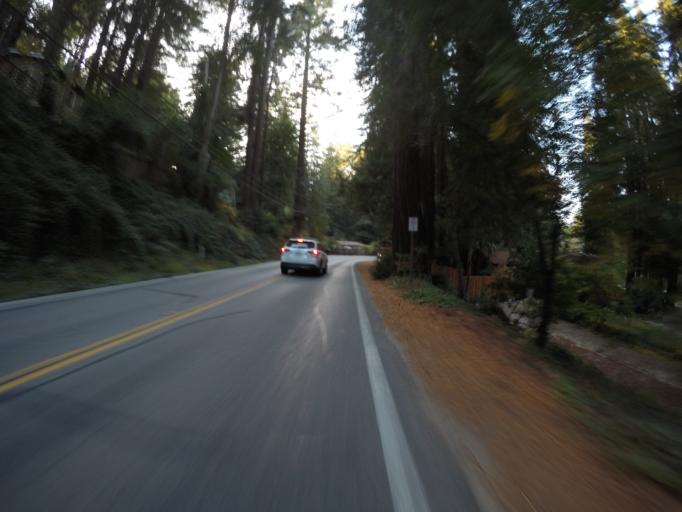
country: US
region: California
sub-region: Santa Cruz County
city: Felton
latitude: 37.0387
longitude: -122.0685
